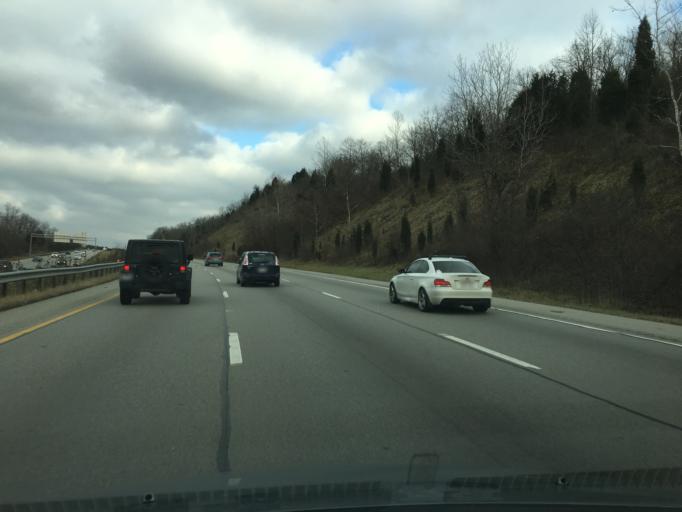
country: US
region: Ohio
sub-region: Hamilton County
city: Miamitown
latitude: 39.2165
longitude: -84.6715
